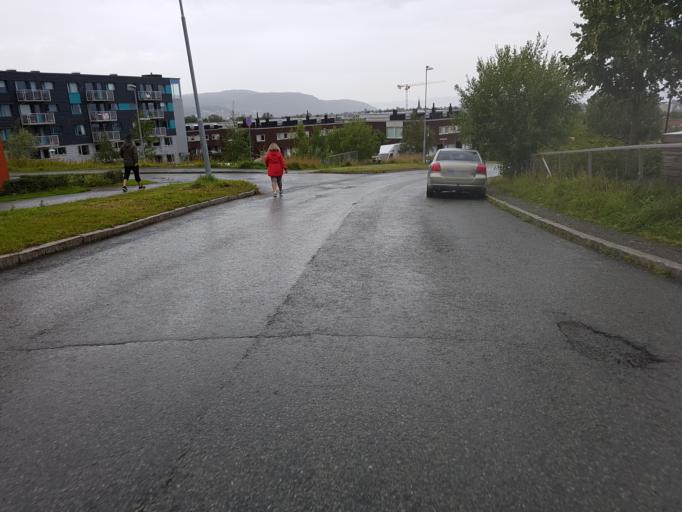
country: NO
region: Sor-Trondelag
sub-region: Trondheim
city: Trondheim
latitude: 63.4092
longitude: 10.4561
